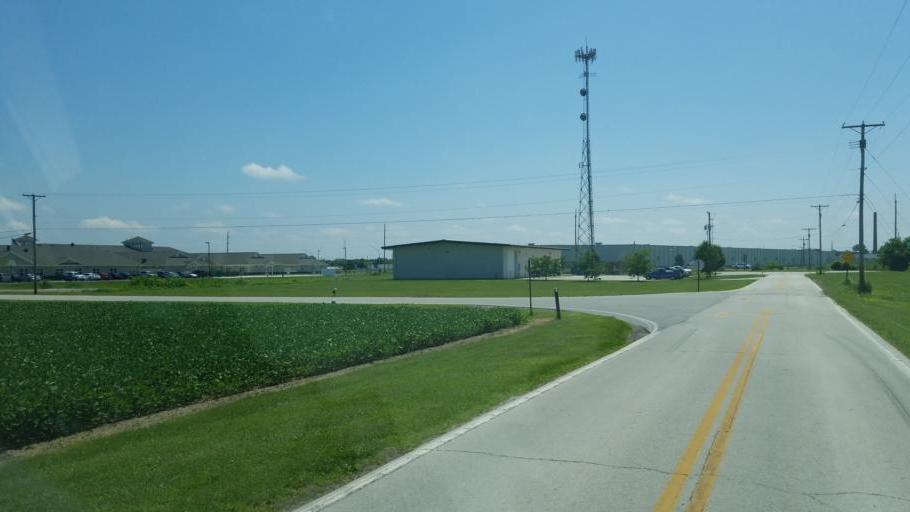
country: US
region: Ohio
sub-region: Sandusky County
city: Fremont
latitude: 41.3672
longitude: -83.0927
